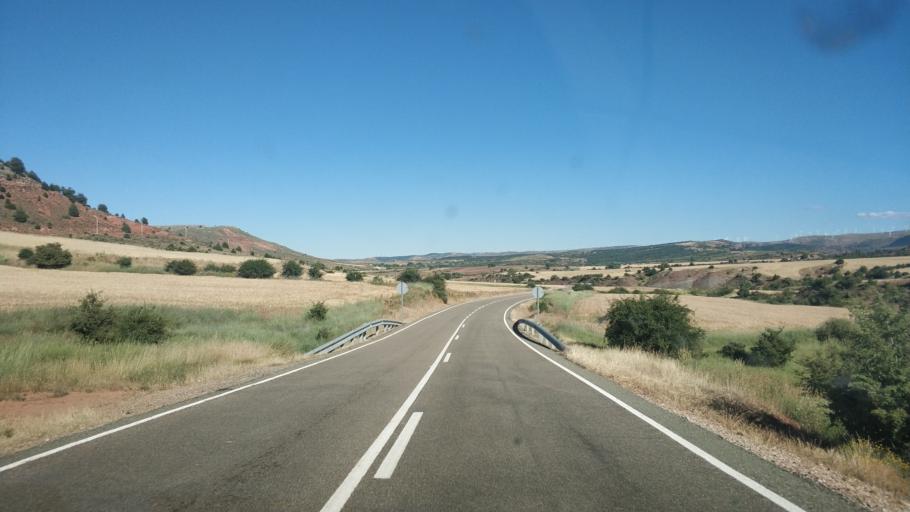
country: ES
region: Castille and Leon
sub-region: Provincia de Soria
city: Montejo de Tiermes
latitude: 41.3501
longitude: -3.1630
